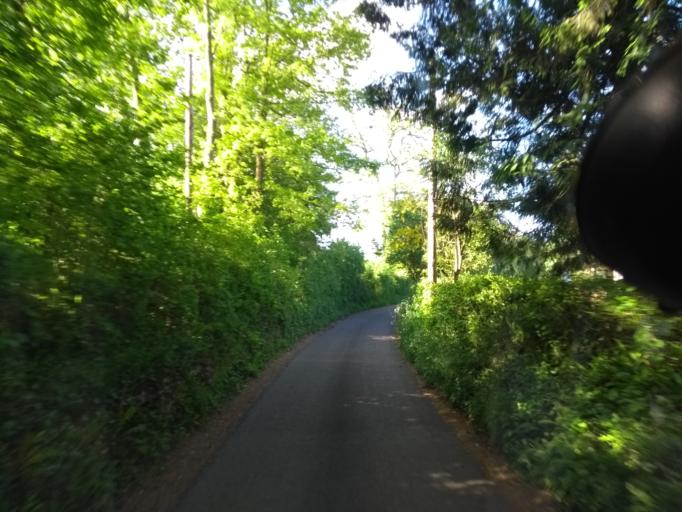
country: GB
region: England
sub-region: Somerset
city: Taunton
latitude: 50.9714
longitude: -3.1055
